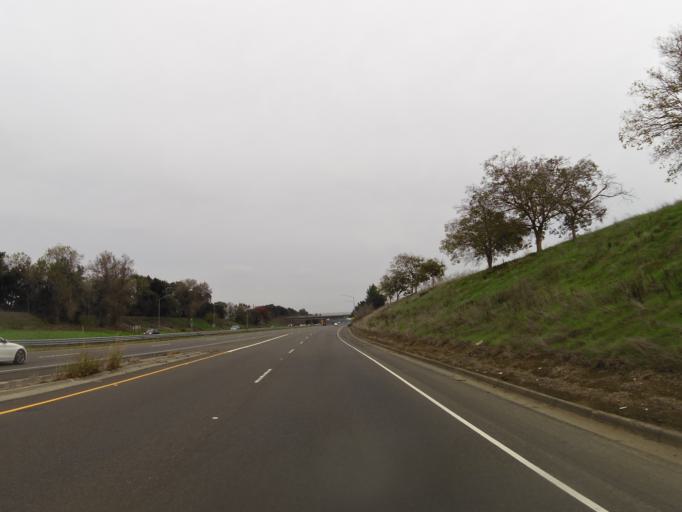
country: US
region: California
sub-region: Yolo County
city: Davis
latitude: 38.5283
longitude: -121.7685
